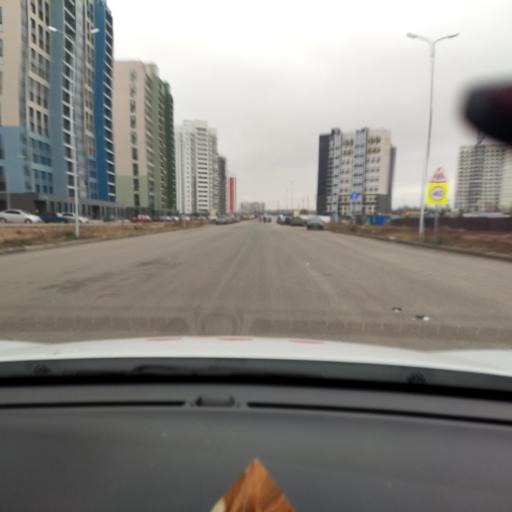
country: RU
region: Tatarstan
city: Osinovo
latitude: 55.8569
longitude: 48.9075
